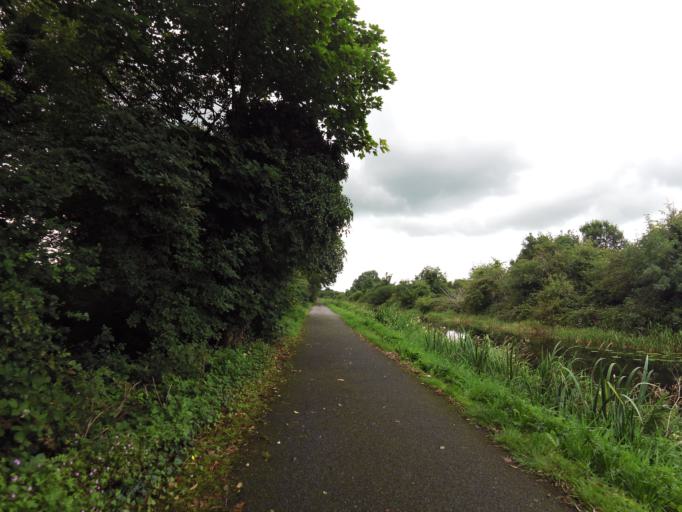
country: IE
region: Leinster
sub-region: An Iarmhi
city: An Muileann gCearr
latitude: 53.5097
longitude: -7.3921
